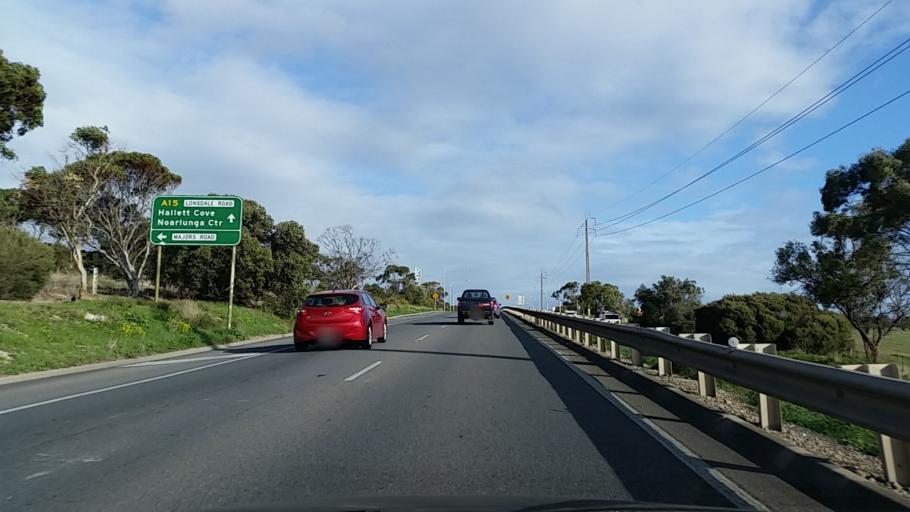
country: AU
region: South Australia
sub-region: Adelaide Hills
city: Seacliff
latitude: -35.0522
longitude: 138.5348
